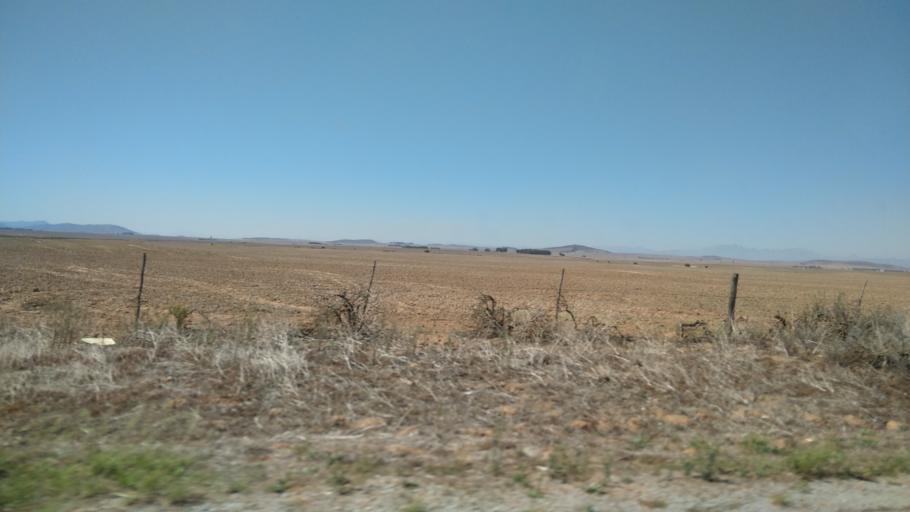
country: ZA
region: Western Cape
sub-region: West Coast District Municipality
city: Moorreesburg
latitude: -33.2313
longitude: 18.5585
